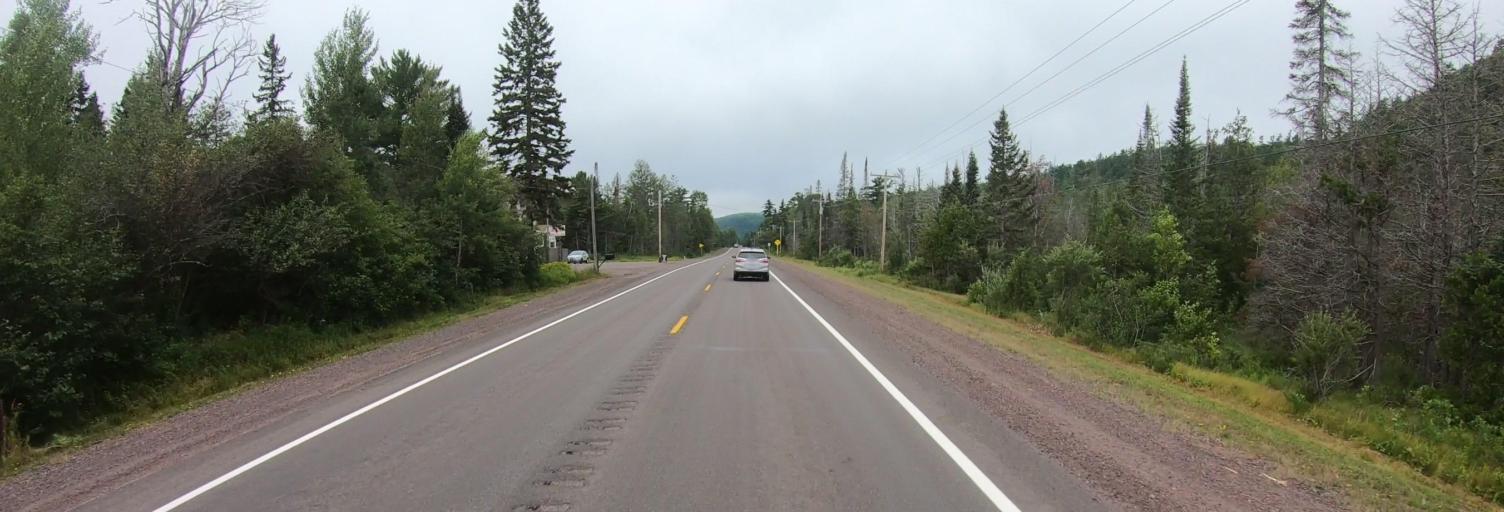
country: US
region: Michigan
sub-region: Keweenaw County
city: Eagle River
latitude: 47.3808
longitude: -88.2973
